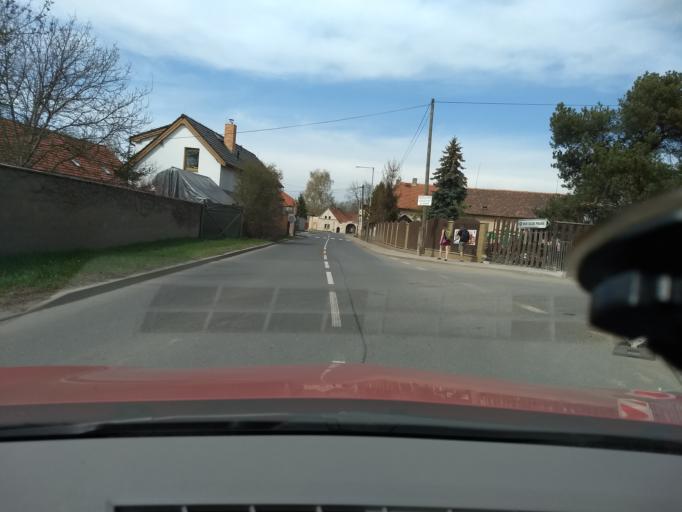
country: CZ
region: Central Bohemia
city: Hostivice
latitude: 50.0632
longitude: 14.2711
